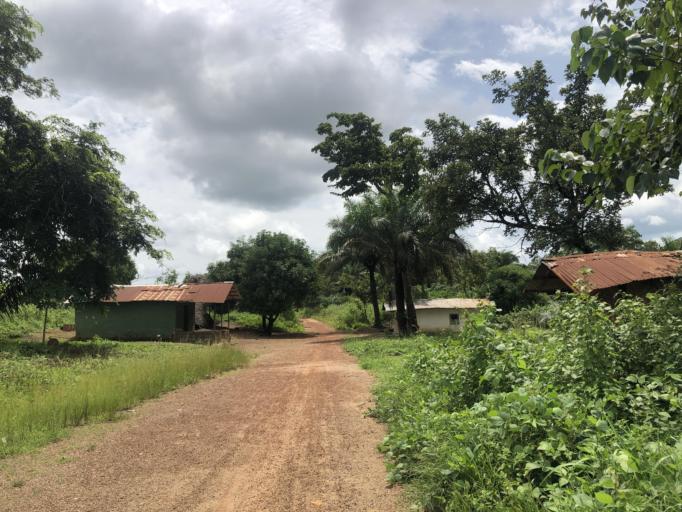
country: SL
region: Northern Province
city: Bumbuna
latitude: 8.9996
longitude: -11.7630
